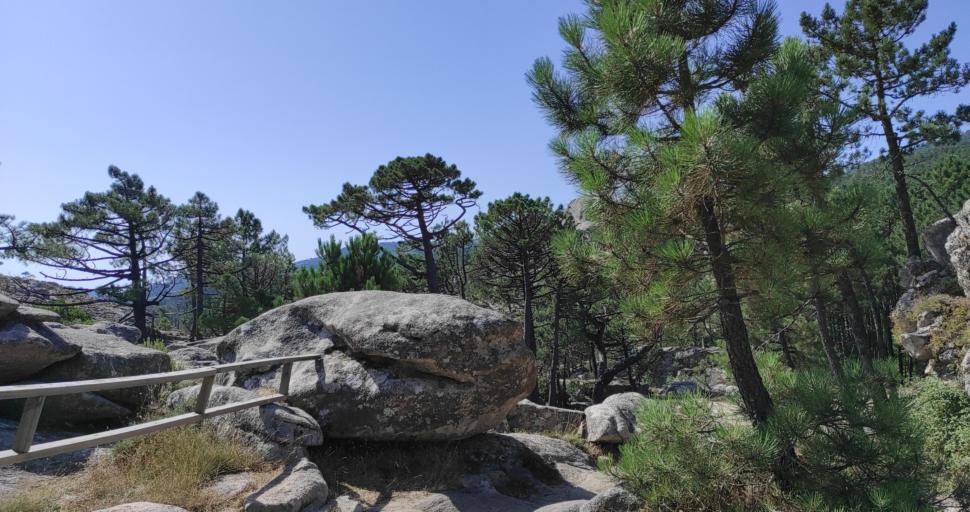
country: FR
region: Corsica
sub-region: Departement de la Corse-du-Sud
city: Zonza
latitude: 41.6872
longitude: 9.2006
